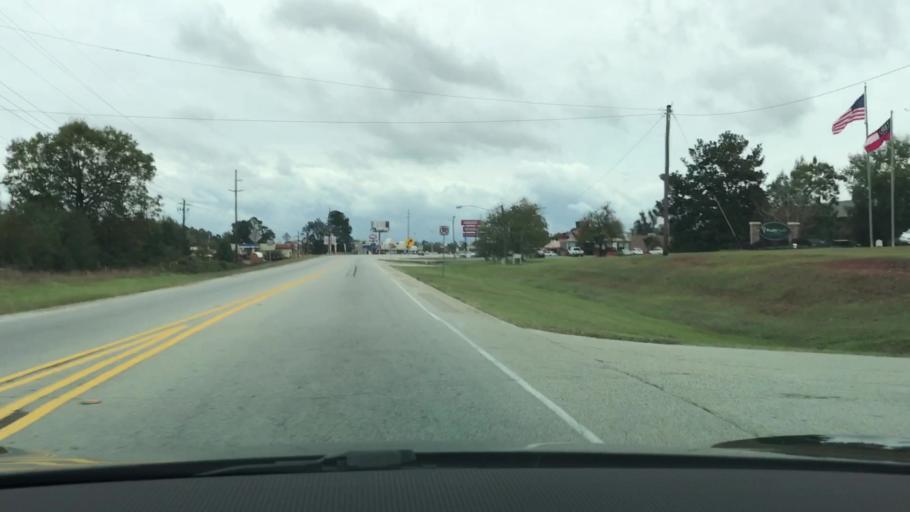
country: US
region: Georgia
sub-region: Jefferson County
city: Louisville
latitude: 33.0130
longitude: -82.4011
